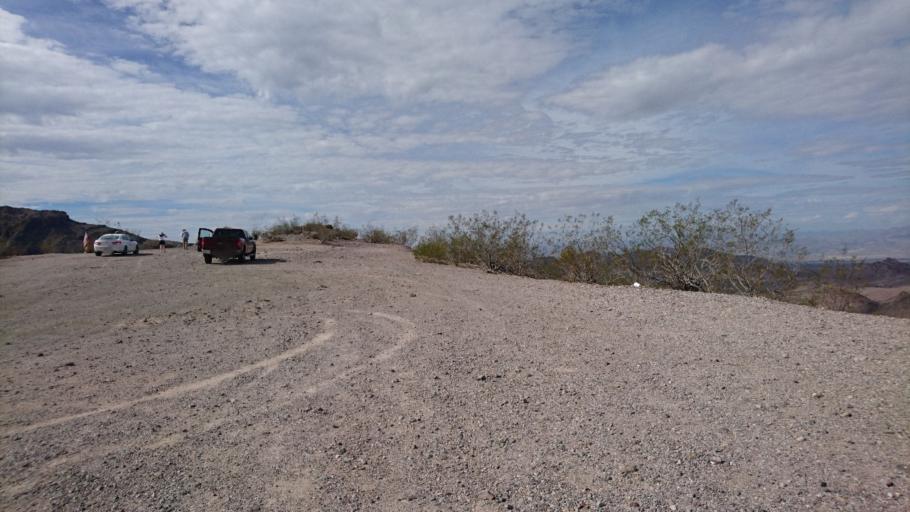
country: US
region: Arizona
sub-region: Mohave County
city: Golden Valley
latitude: 35.0472
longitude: -114.3632
